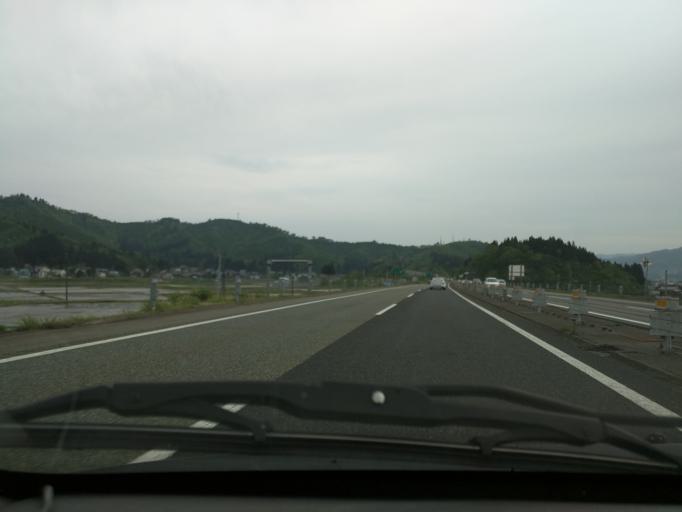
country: JP
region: Niigata
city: Muikamachi
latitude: 37.2095
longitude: 138.9704
